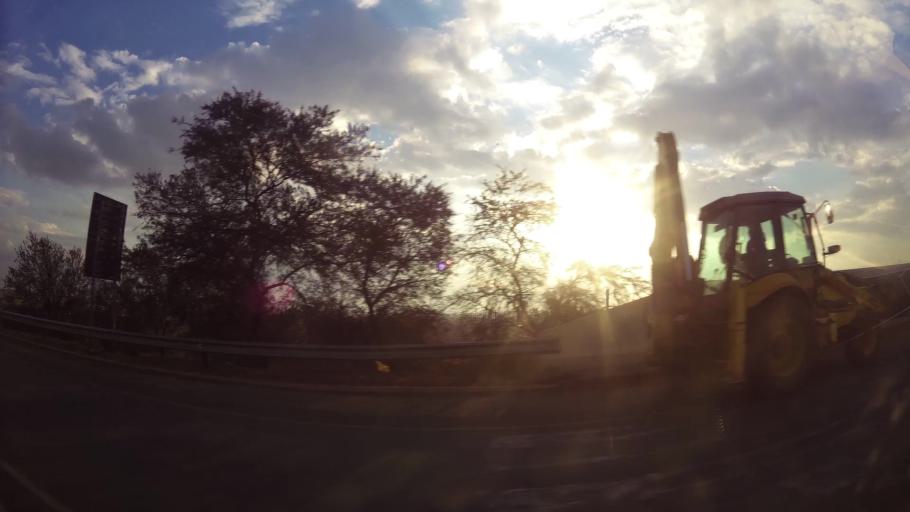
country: ZA
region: Gauteng
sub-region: Sedibeng District Municipality
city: Vanderbijlpark
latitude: -26.6065
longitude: 27.8166
